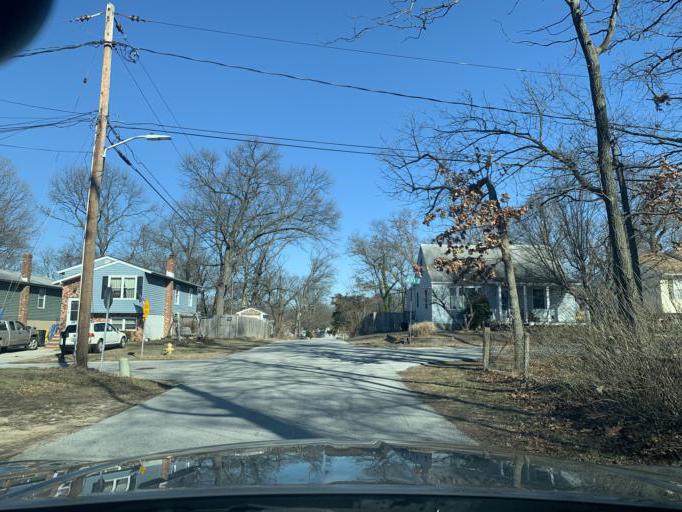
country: US
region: Maryland
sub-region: Anne Arundel County
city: Glen Burnie
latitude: 39.1594
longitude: -76.6347
